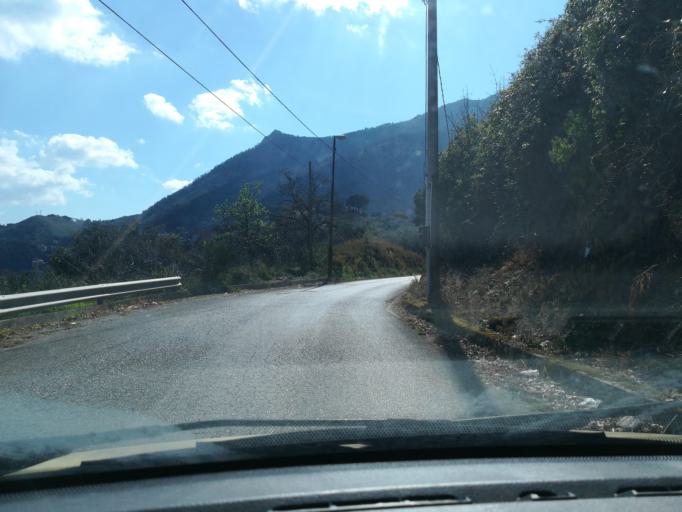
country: IT
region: Sicily
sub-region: Palermo
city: Altofonte
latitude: 38.0440
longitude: 13.2839
